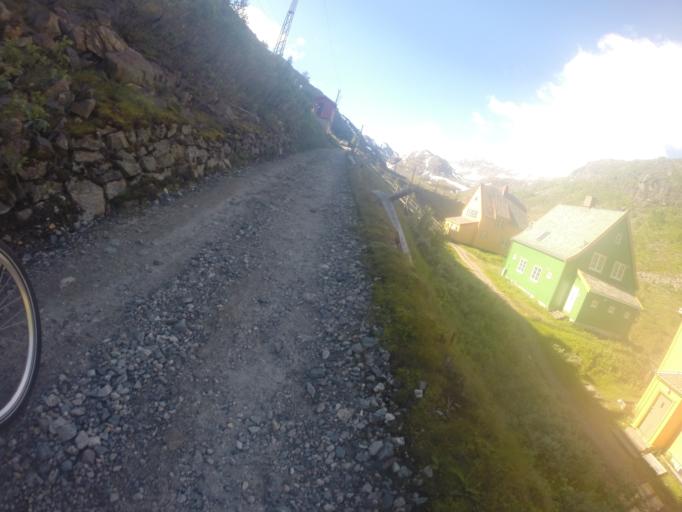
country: NO
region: Sogn og Fjordane
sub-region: Aurland
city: Aurlandsvangen
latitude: 60.7355
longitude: 7.1222
